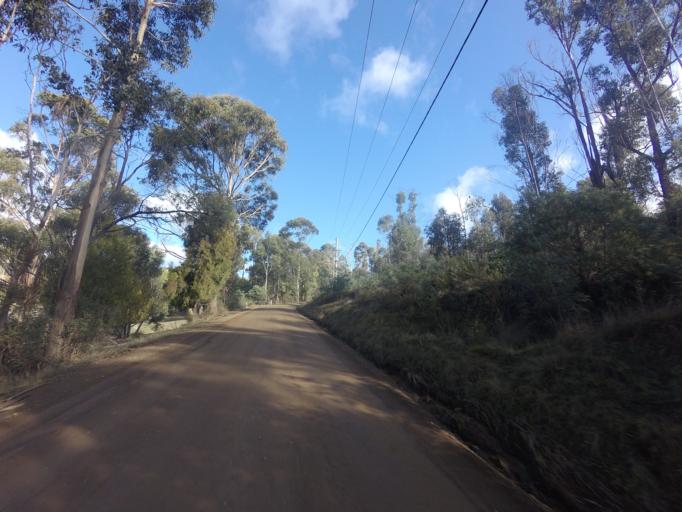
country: AU
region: Tasmania
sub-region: Derwent Valley
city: New Norfolk
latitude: -42.8195
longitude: 147.1240
